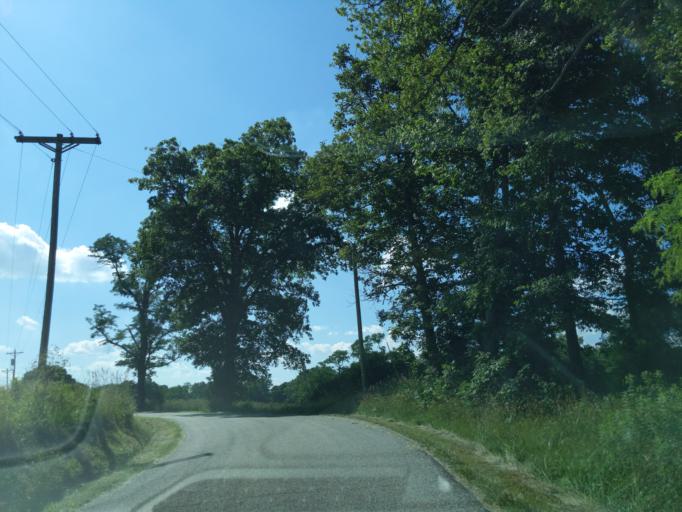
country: US
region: Indiana
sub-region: Ripley County
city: Osgood
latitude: 39.1905
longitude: -85.4194
